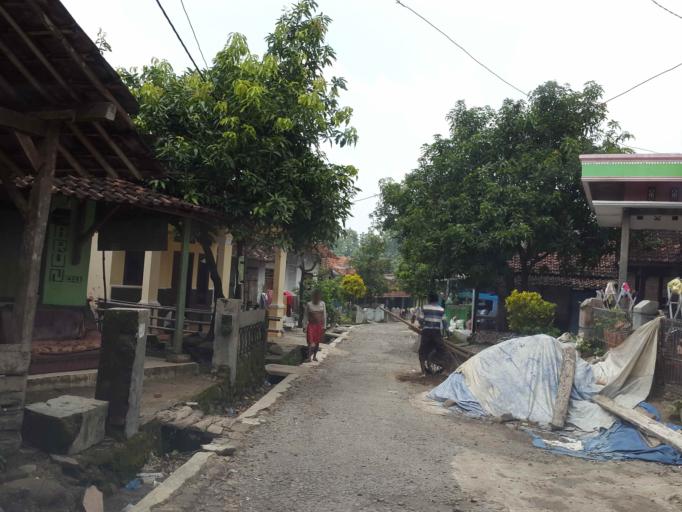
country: ID
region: Central Java
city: Pamedaran
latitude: -7.0690
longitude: 108.8637
